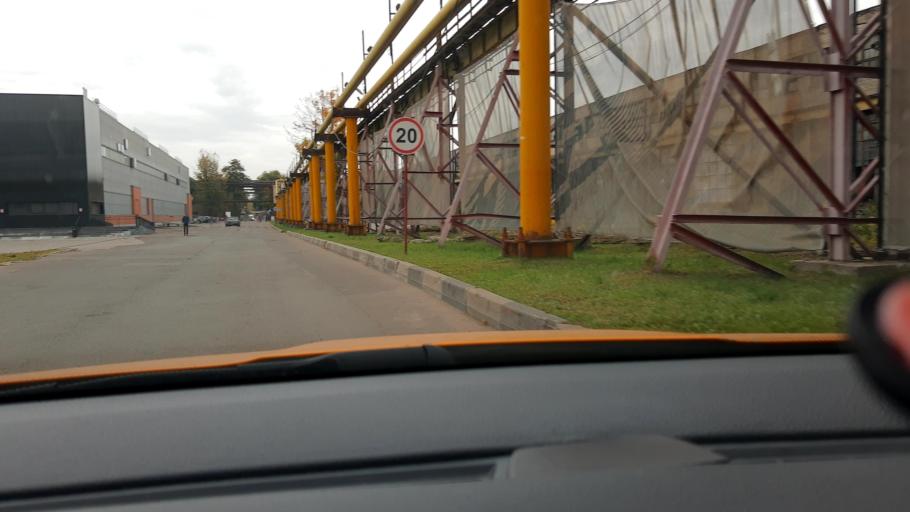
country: RU
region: Moscow
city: Taganskiy
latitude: 55.7212
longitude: 37.6832
